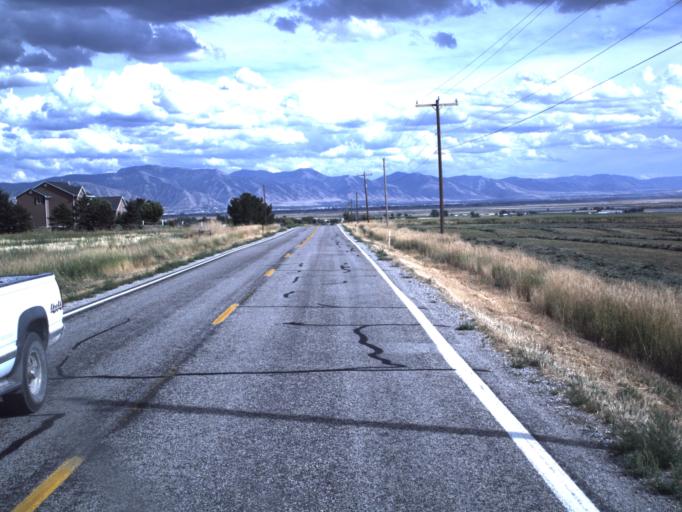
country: US
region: Utah
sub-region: Cache County
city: Benson
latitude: 41.8687
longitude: -112.0115
